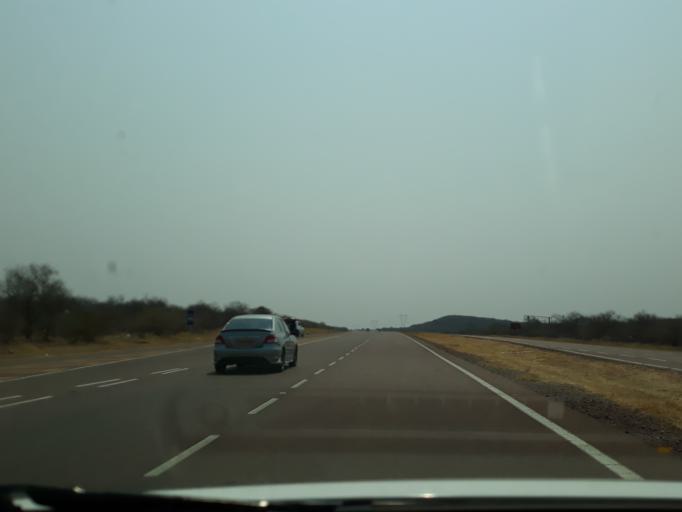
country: BW
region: Kgatleng
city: Bokaa
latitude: -24.4017
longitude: 26.0562
